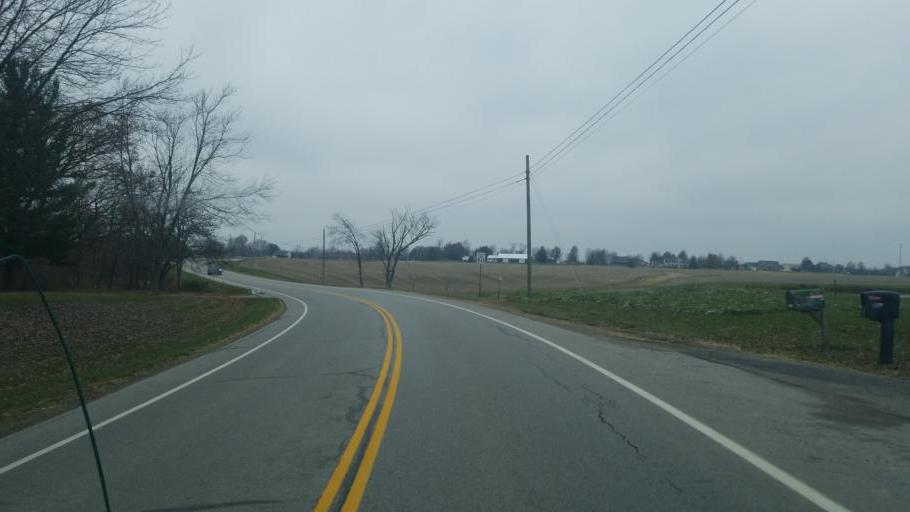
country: US
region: Ohio
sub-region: Medina County
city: Medina
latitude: 41.1494
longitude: -81.9236
